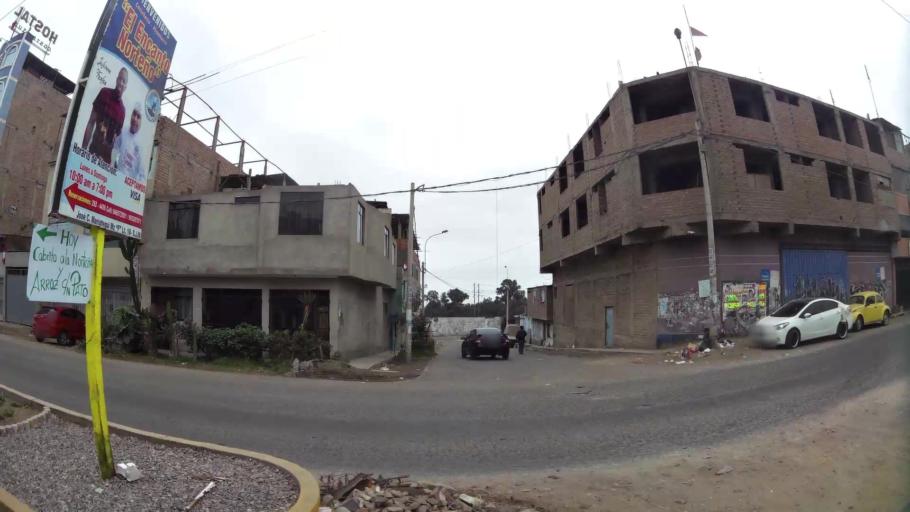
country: PE
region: Lima
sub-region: Lima
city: Surco
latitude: -12.1904
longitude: -76.9622
